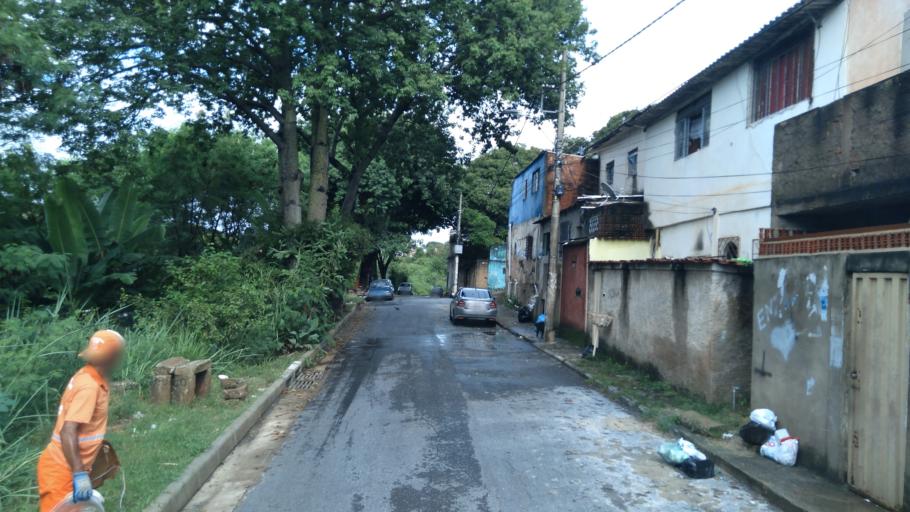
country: BR
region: Minas Gerais
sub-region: Belo Horizonte
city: Belo Horizonte
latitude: -19.9018
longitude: -43.9030
